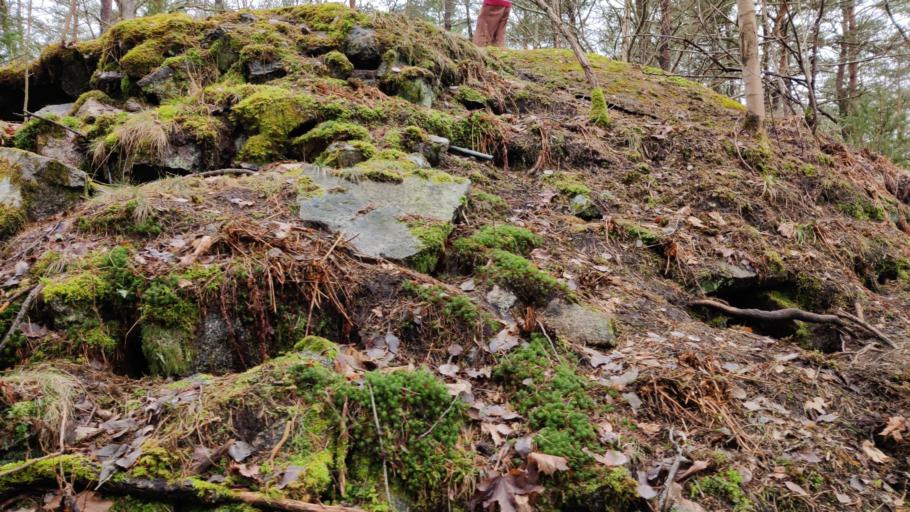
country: SE
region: Vaestra Goetaland
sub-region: Uddevalla Kommun
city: Uddevalla
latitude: 58.3431
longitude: 11.9378
